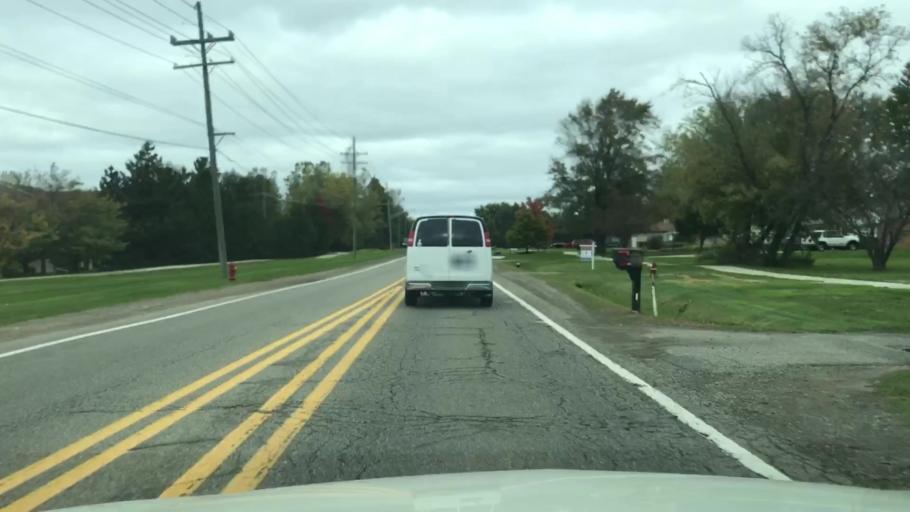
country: US
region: Michigan
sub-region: Oakland County
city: Rochester
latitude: 42.6825
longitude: -83.0941
